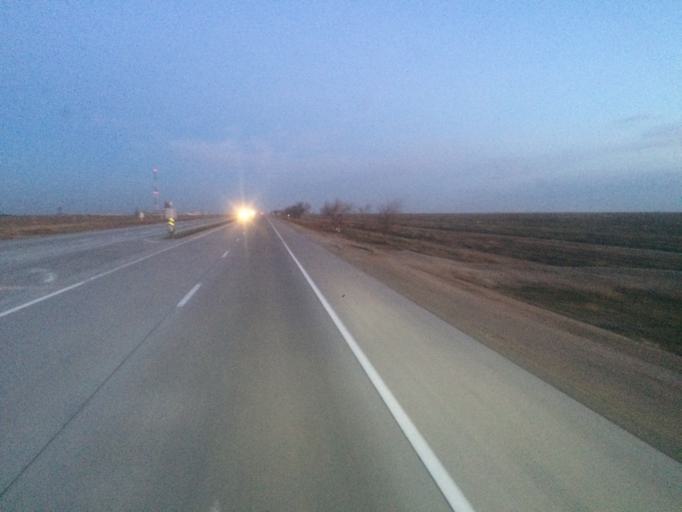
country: KZ
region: Ongtustik Qazaqstan
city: Temirlanovka
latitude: 42.8341
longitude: 69.1200
